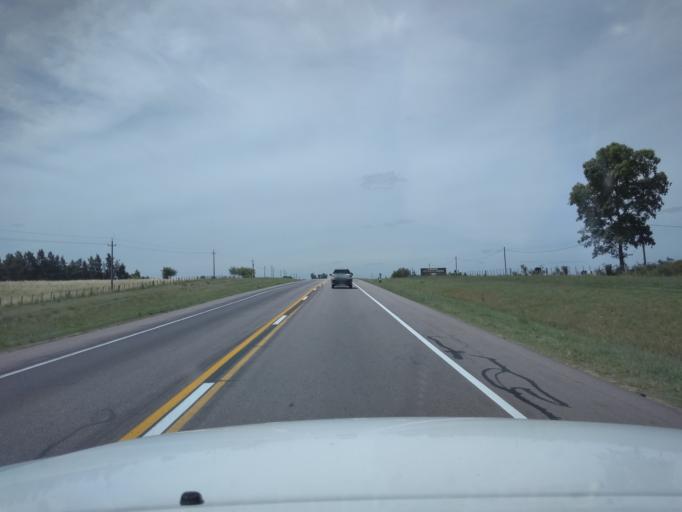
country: UY
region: Florida
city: Florida
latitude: -34.1782
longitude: -56.1911
